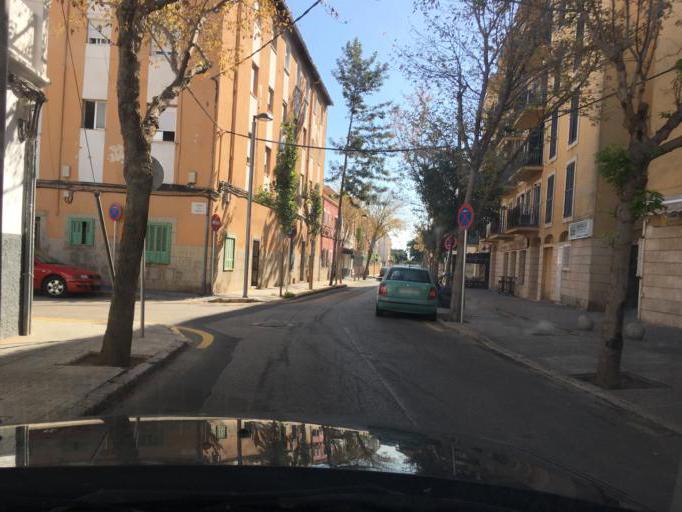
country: ES
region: Balearic Islands
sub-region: Illes Balears
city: Palma
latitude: 39.5839
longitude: 2.6765
